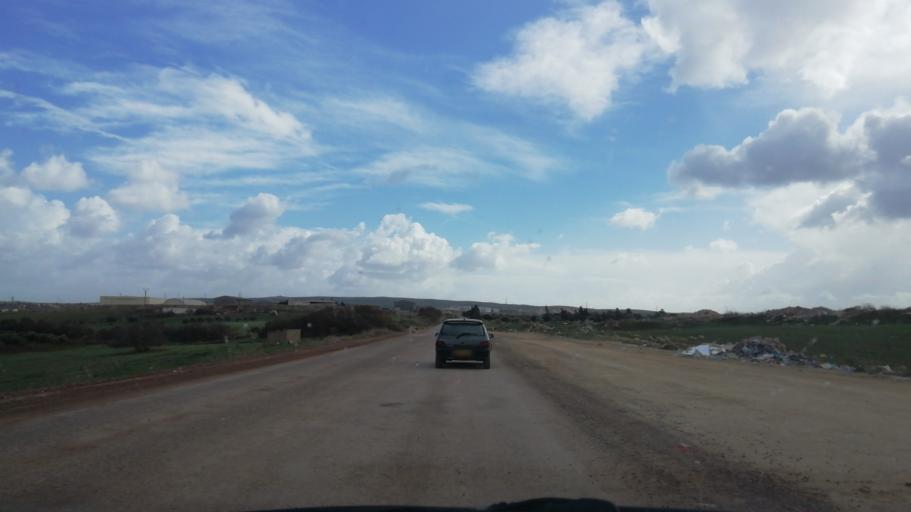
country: DZ
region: Oran
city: Sidi ech Chahmi
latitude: 35.6351
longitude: -0.5369
